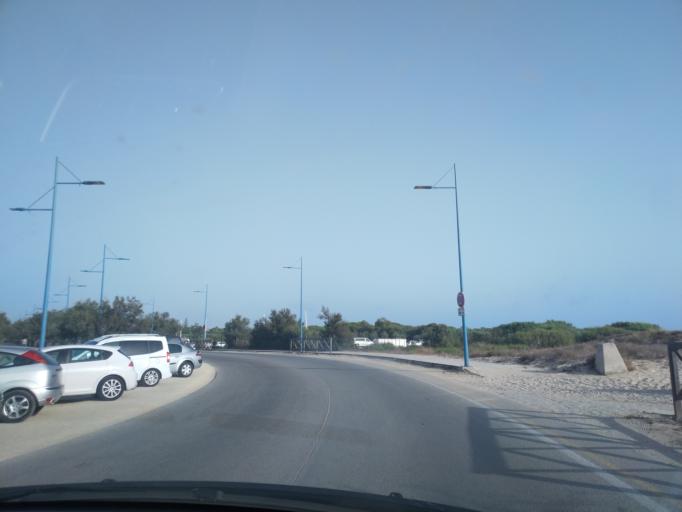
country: ES
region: Andalusia
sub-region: Provincia de Cadiz
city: Chiclana de la Frontera
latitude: 36.3869
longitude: -6.2068
